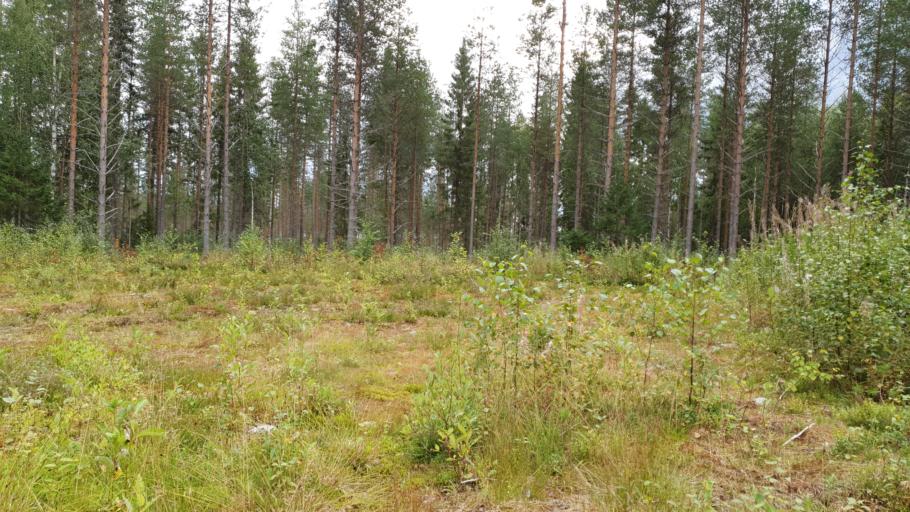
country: FI
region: Kainuu
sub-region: Kehys-Kainuu
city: Kuhmo
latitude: 64.1350
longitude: 29.4109
